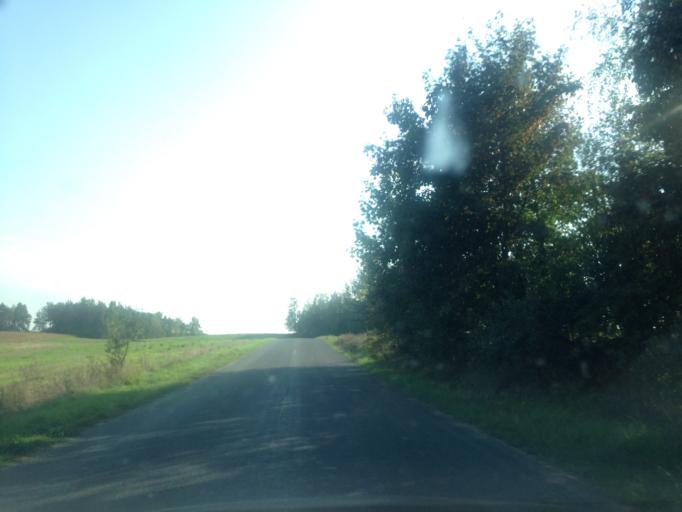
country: PL
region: Kujawsko-Pomorskie
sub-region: Powiat brodnicki
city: Brzozie
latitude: 53.3022
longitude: 19.6854
